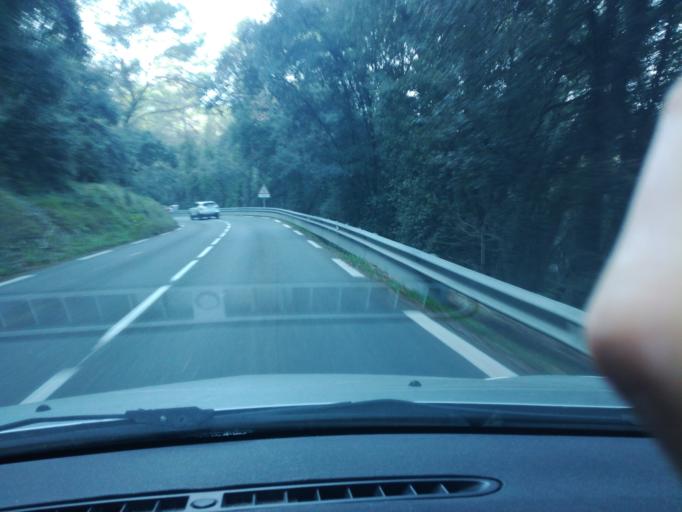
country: FR
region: Provence-Alpes-Cote d'Azur
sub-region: Departement des Alpes-Maritimes
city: Valbonne
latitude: 43.6545
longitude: 7.0063
